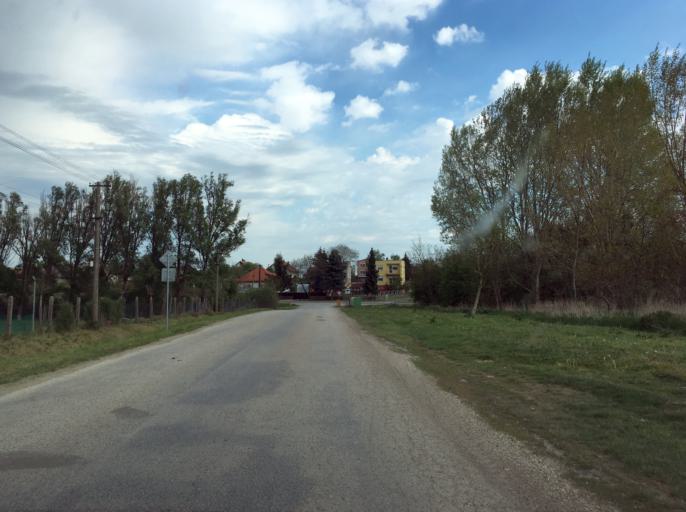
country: SK
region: Nitriansky
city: Svodin
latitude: 47.8953
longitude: 18.4116
